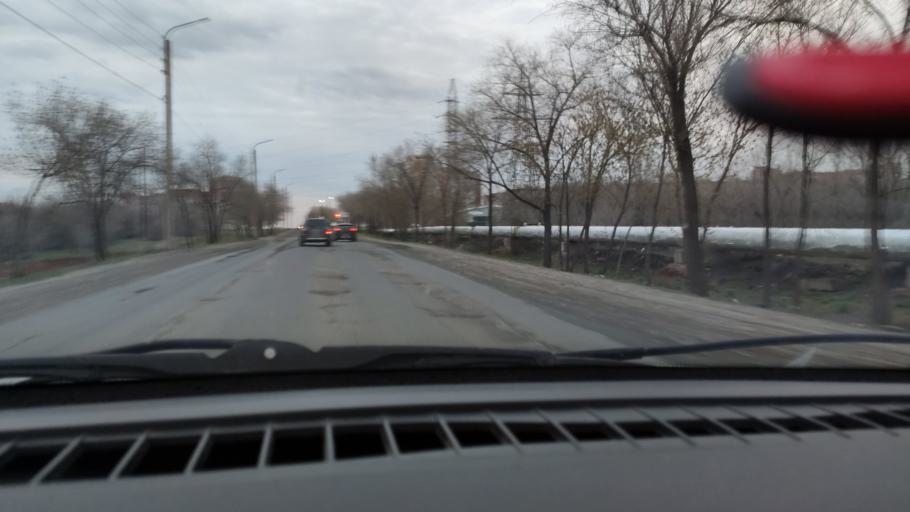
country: RU
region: Orenburg
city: Orenburg
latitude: 51.8204
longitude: 55.1578
